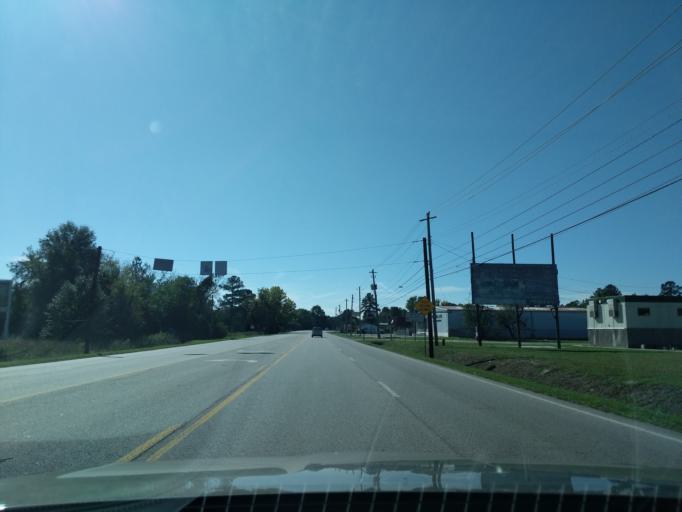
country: US
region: Georgia
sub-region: Richmond County
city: Augusta
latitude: 33.4272
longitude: -82.0062
